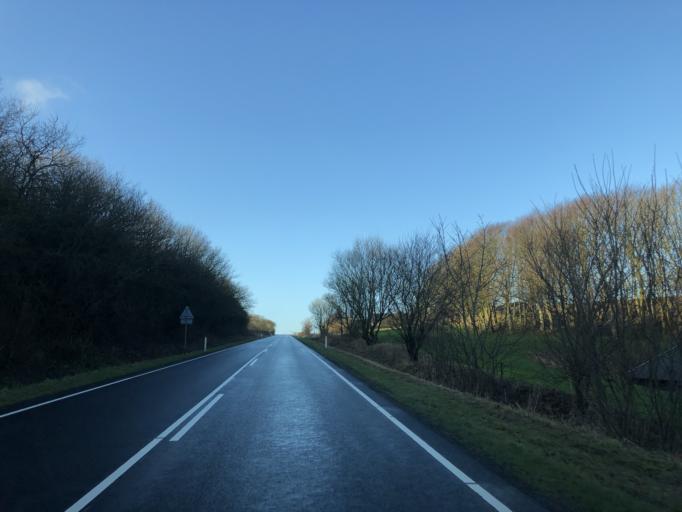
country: DK
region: Central Jutland
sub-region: Lemvig Kommune
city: Lemvig
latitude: 56.5586
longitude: 8.4331
